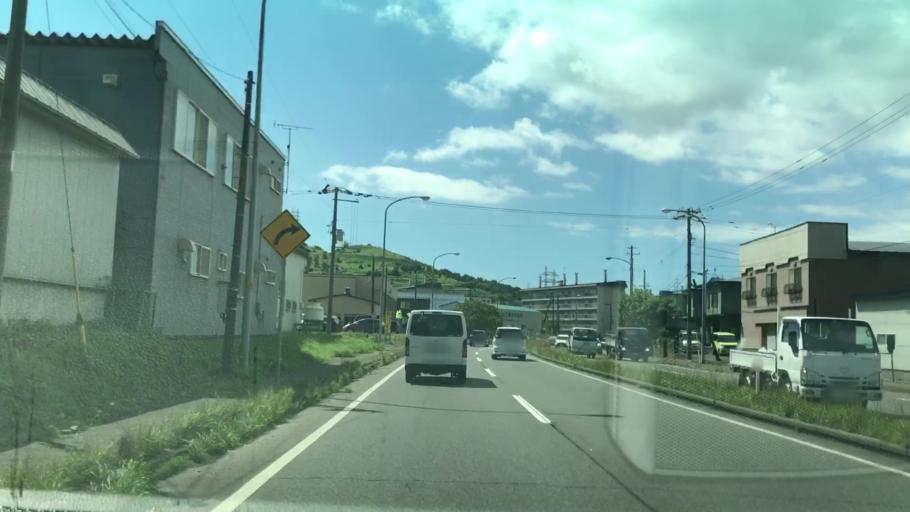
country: JP
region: Hokkaido
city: Muroran
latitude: 42.3380
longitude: 141.0247
